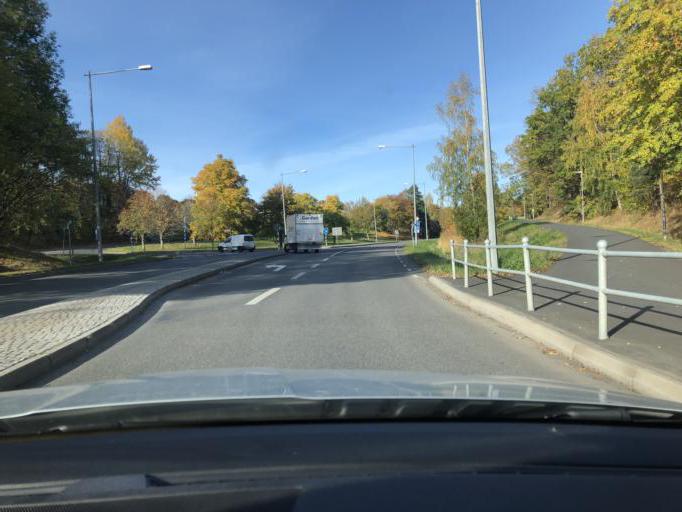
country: SE
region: Joenkoeping
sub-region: Jonkopings Kommun
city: Jonkoping
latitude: 57.7723
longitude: 14.1316
